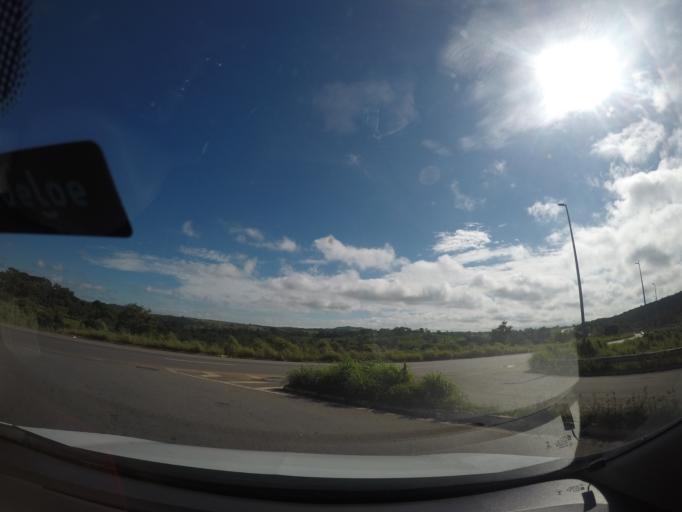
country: BR
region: Goias
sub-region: Senador Canedo
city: Senador Canedo
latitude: -16.6835
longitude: -49.1317
